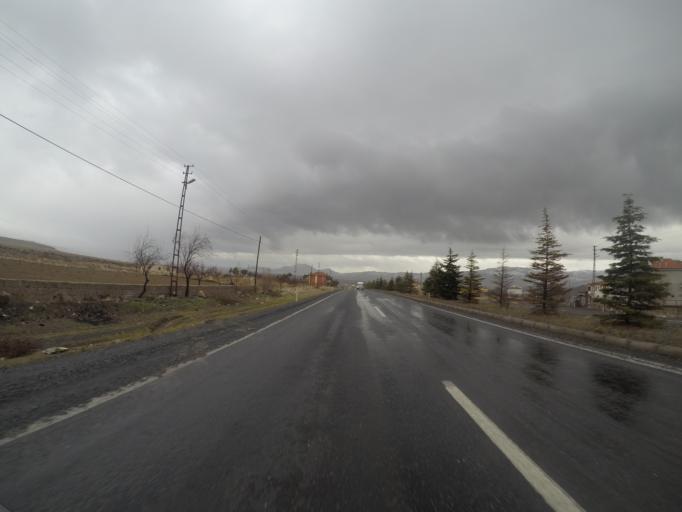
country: TR
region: Kayseri
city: Incesu
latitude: 38.6810
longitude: 35.2208
